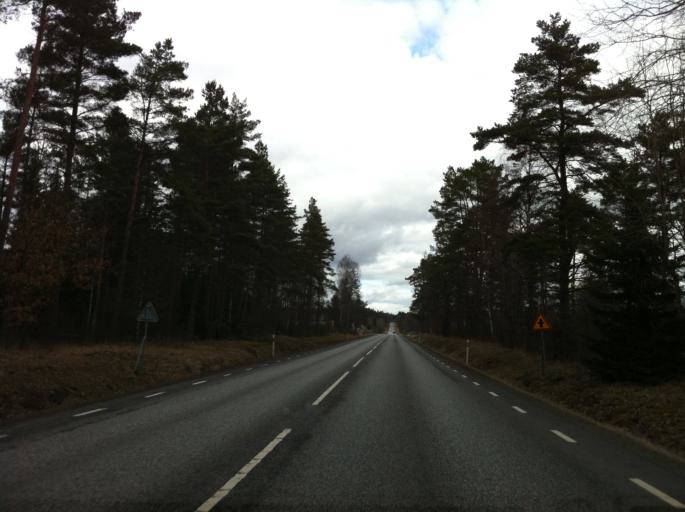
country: SE
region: Vaestra Goetaland
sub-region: Tranemo Kommun
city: Limmared
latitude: 57.5712
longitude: 13.4131
